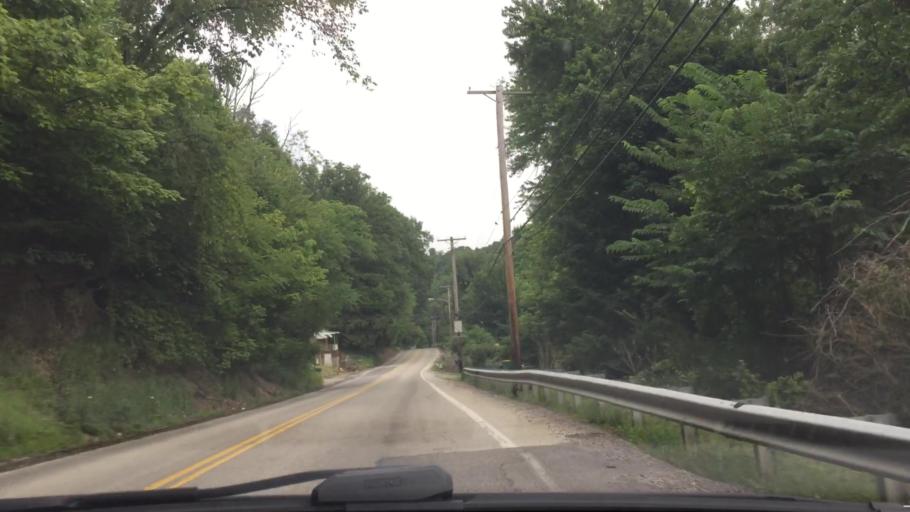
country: US
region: Pennsylvania
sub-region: Allegheny County
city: Rennerdale
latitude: 40.3758
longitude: -80.1359
